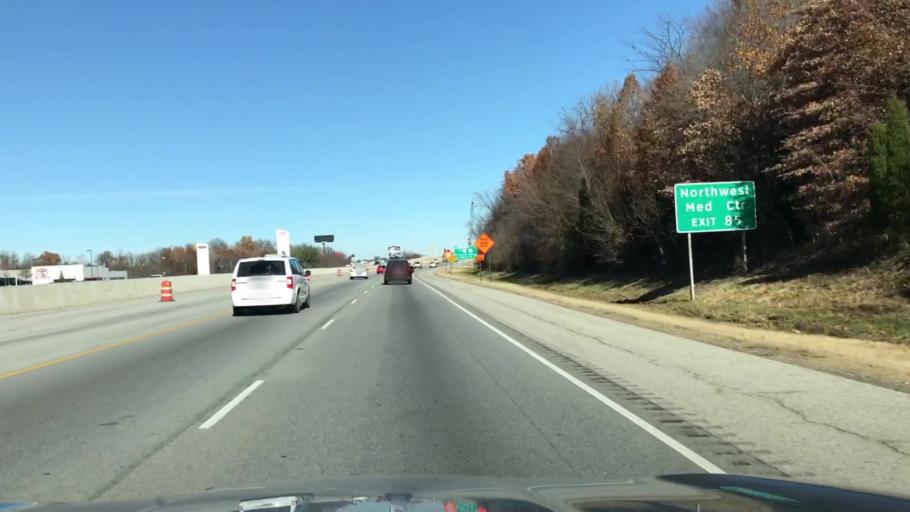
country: US
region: Arkansas
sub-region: Benton County
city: Bentonville
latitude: 36.3290
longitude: -94.1845
